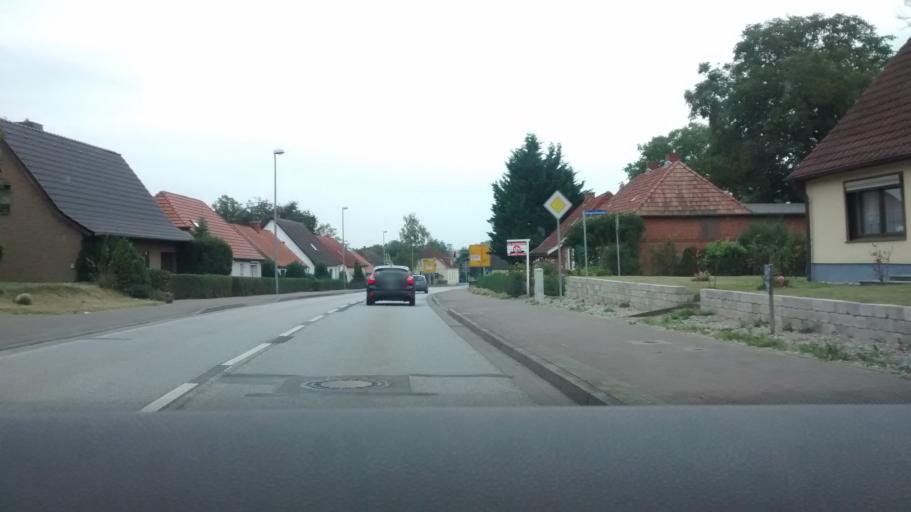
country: DE
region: Mecklenburg-Vorpommern
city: Mecklenburg
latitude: 53.8436
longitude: 11.4598
